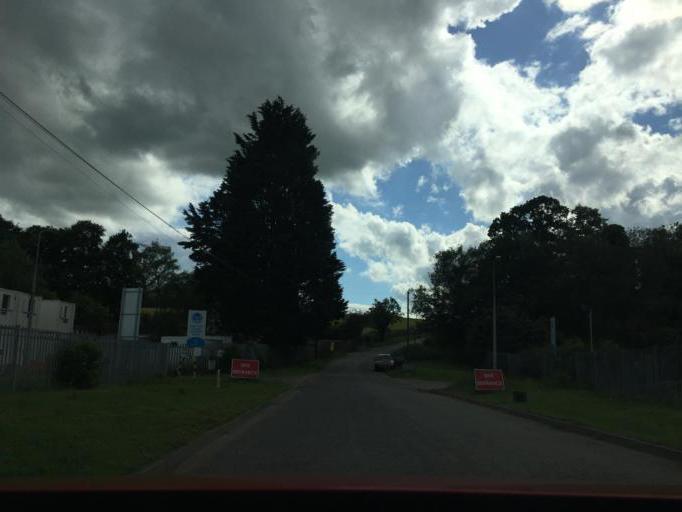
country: GB
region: England
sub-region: Hertfordshire
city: Harpenden
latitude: 51.8498
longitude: -0.3751
